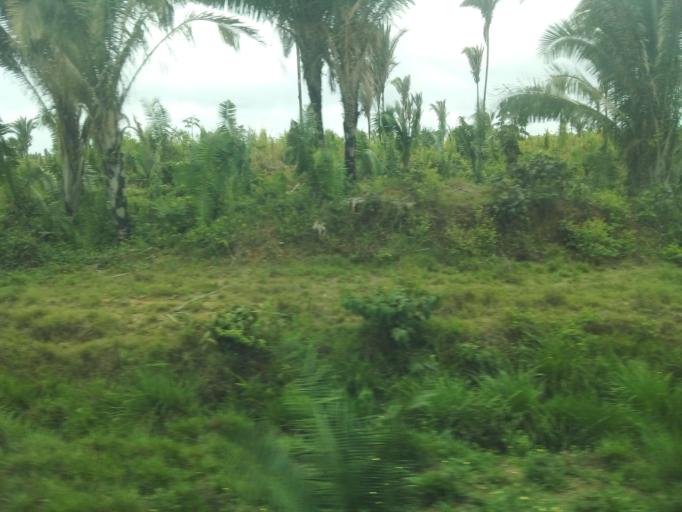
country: BR
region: Maranhao
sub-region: Moncao
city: Moncao
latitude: -3.5847
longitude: -45.0923
